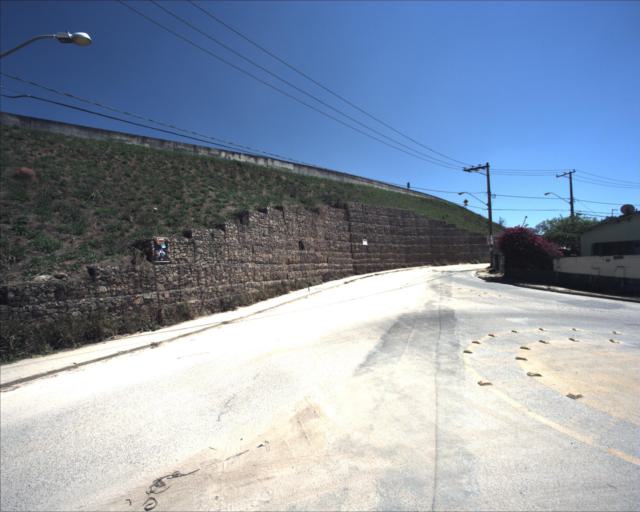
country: BR
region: Sao Paulo
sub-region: Votorantim
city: Votorantim
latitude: -23.5022
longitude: -47.3707
